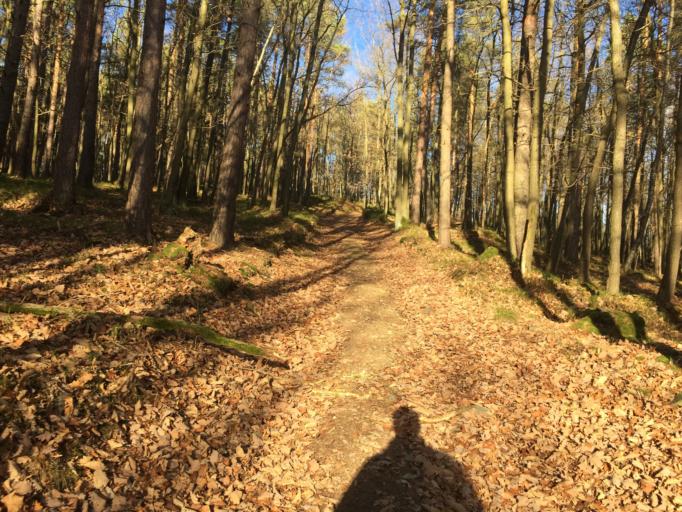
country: DE
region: Thuringia
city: Bad Blankenburg
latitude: 50.6601
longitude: 11.2726
